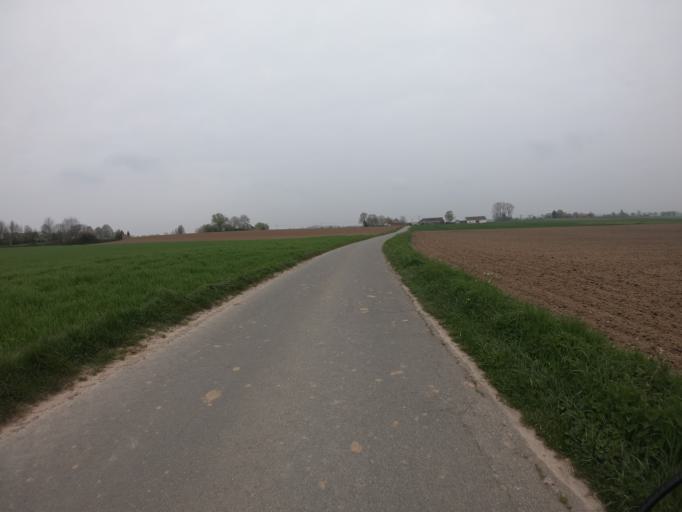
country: BE
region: Wallonia
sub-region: Province du Hainaut
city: Flobecq
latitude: 50.7562
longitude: 3.7768
